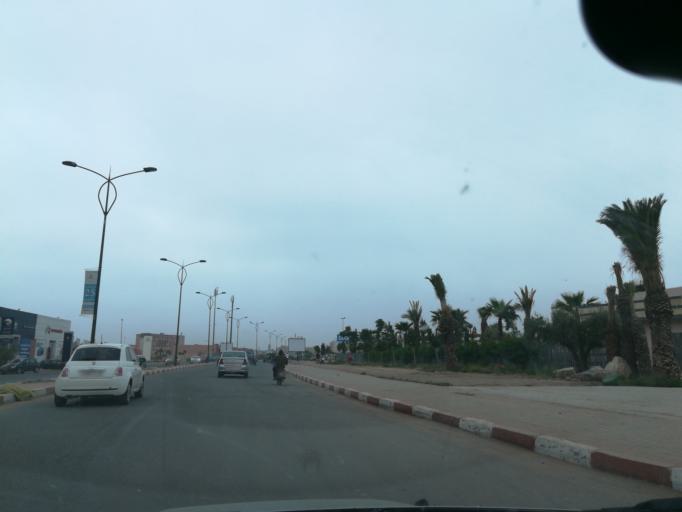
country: MA
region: Marrakech-Tensift-Al Haouz
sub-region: Marrakech
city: Marrakesh
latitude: 31.6717
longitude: -8.0144
